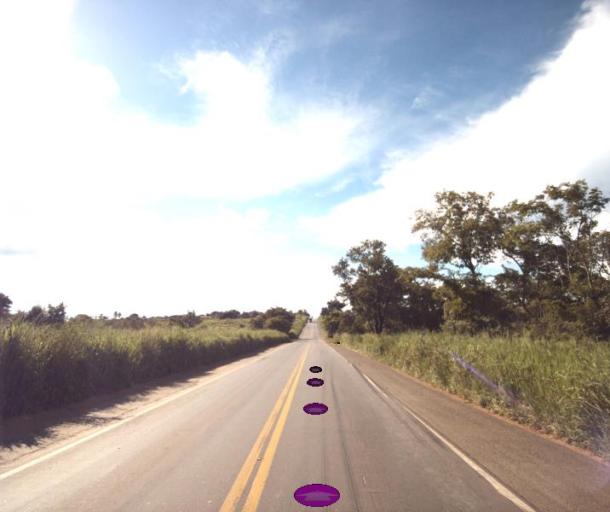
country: BR
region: Goias
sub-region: Rialma
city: Rialma
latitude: -15.4575
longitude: -49.5022
